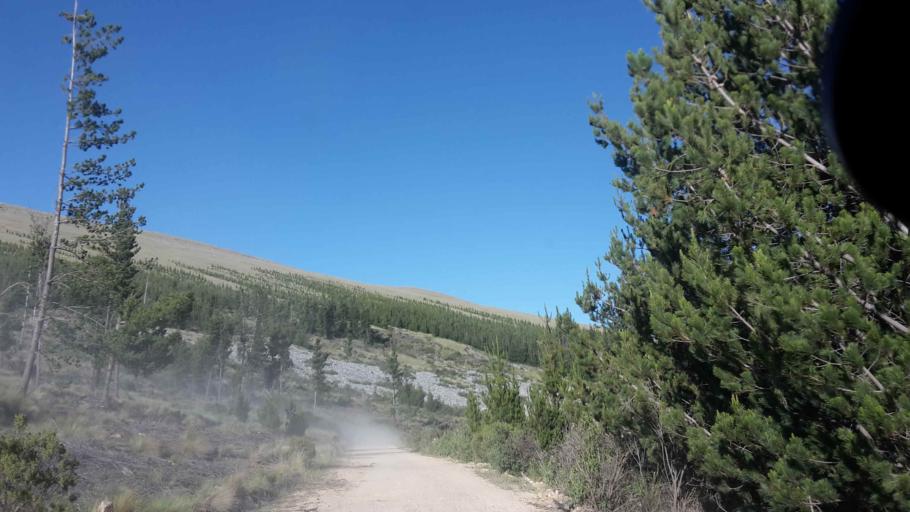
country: BO
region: Cochabamba
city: Arani
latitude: -17.7129
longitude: -65.6851
